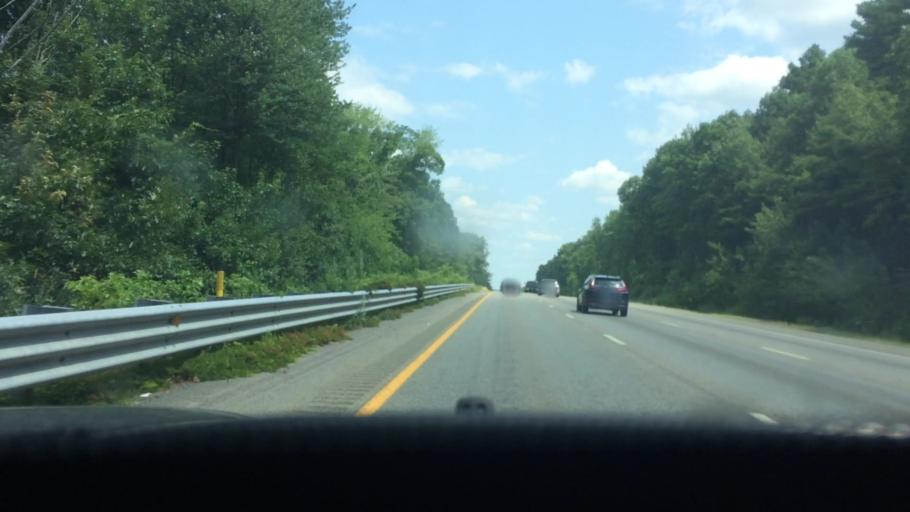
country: US
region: Massachusetts
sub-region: Worcester County
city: Harvard
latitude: 42.5029
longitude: -71.5287
